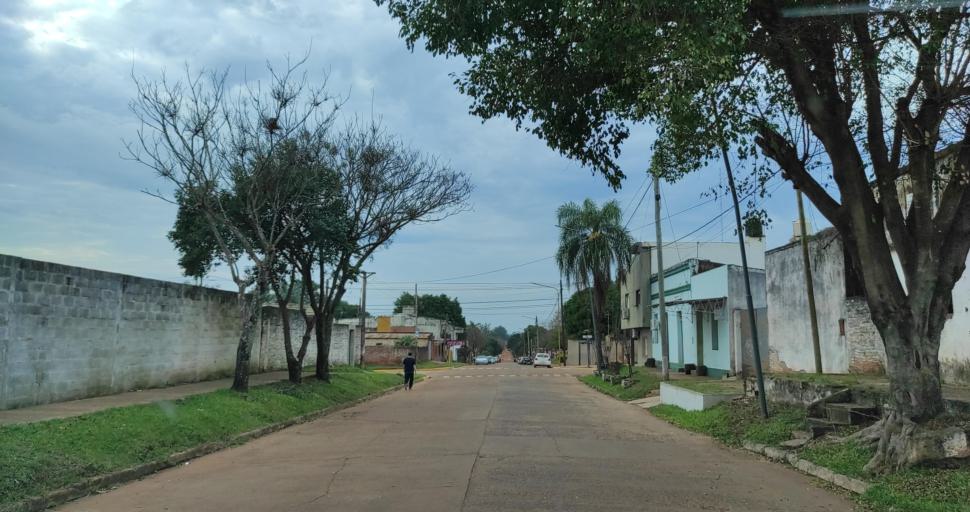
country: AR
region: Corrientes
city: Santo Tome
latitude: -28.5543
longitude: -56.0401
